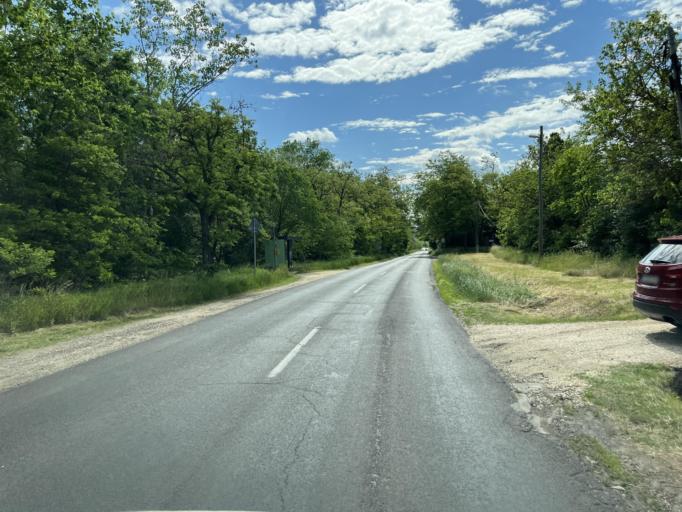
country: HU
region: Pest
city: Godollo
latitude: 47.5832
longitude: 19.3860
